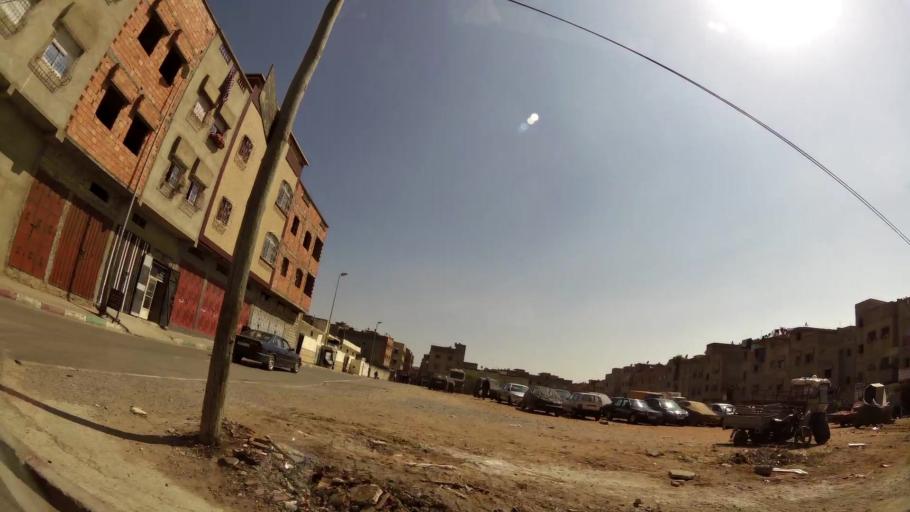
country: MA
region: Rabat-Sale-Zemmour-Zaer
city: Sale
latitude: 34.0697
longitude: -6.7651
